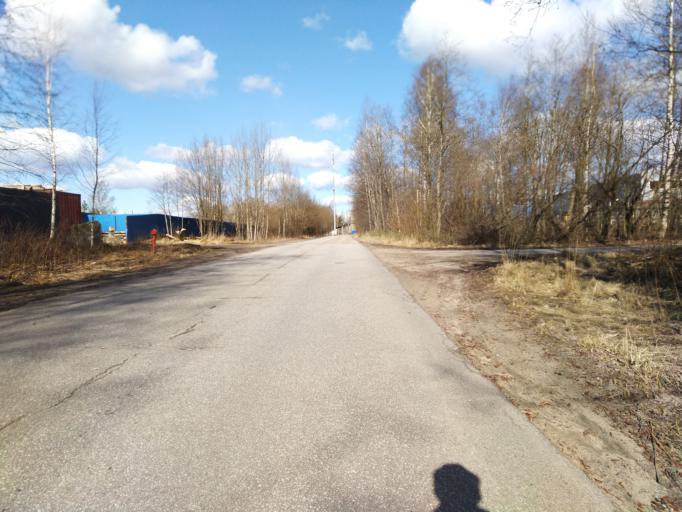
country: RU
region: Leningrad
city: Novoye Devyatkino
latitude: 60.1037
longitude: 30.4803
